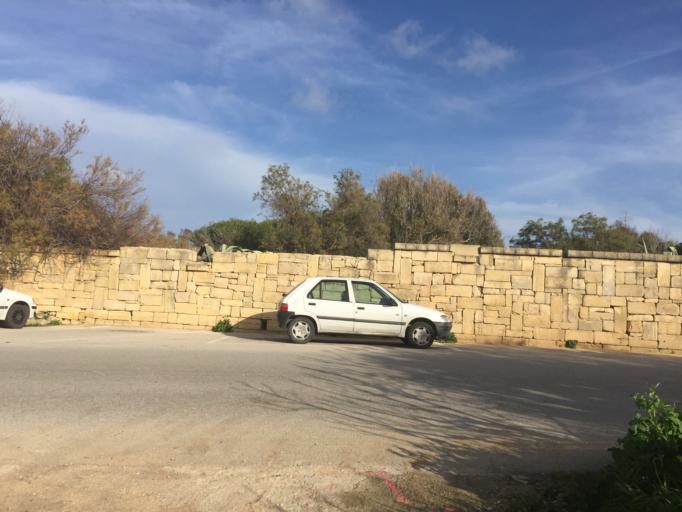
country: MT
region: L-Imgarr
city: Imgarr
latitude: 35.9334
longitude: 14.3463
